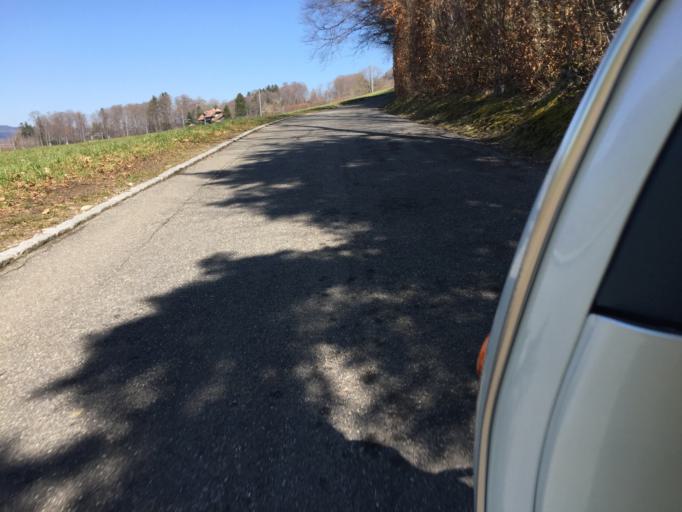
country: CH
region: Bern
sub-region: Bern-Mittelland District
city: Taegertschi
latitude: 46.8901
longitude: 7.5754
